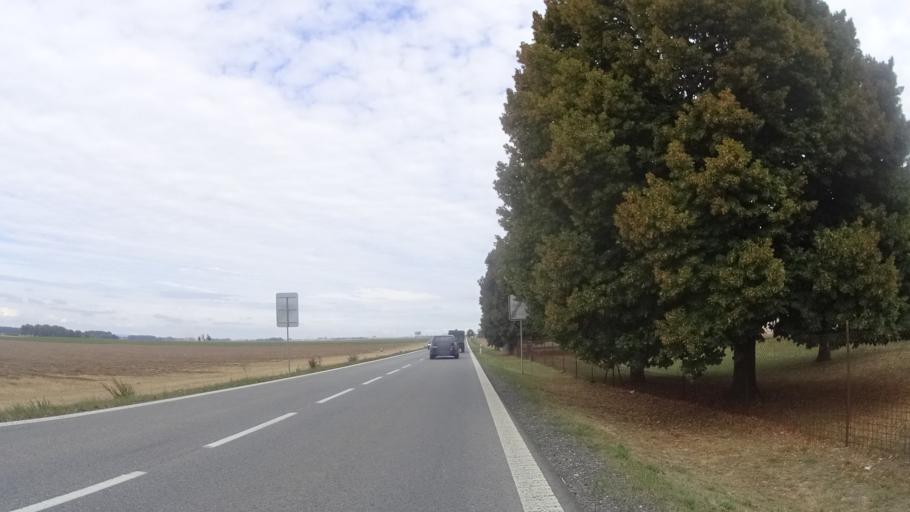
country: CZ
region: Olomoucky
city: Tovacov
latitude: 49.4417
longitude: 17.2806
